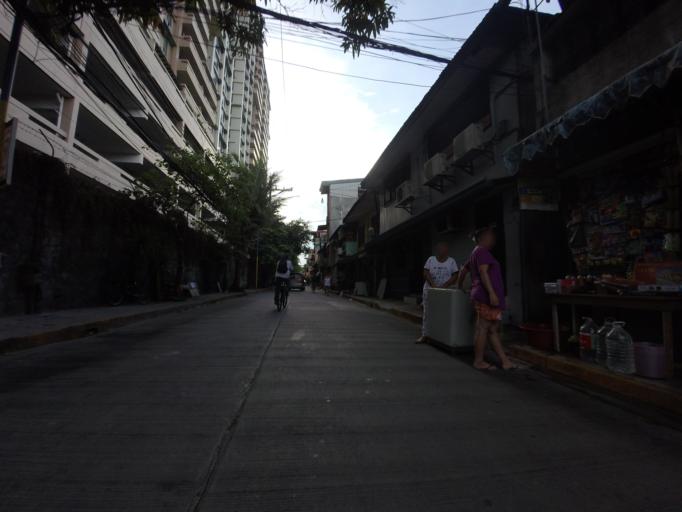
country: PH
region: Metro Manila
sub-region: Mandaluyong
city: Mandaluyong City
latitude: 14.5719
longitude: 121.0324
